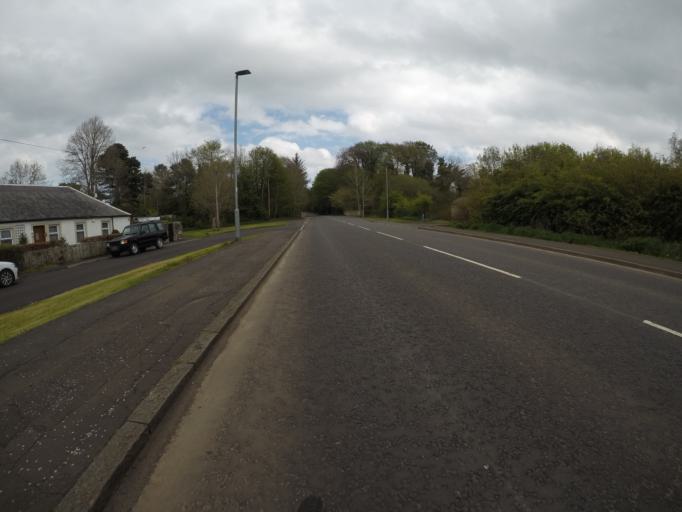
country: GB
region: Scotland
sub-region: North Ayrshire
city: Springside
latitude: 55.6308
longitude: -4.6230
